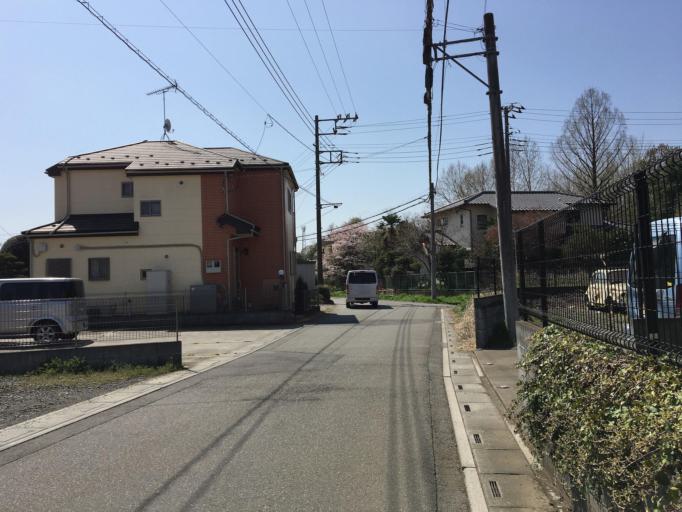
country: JP
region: Saitama
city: Sakado
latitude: 35.9049
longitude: 139.3601
